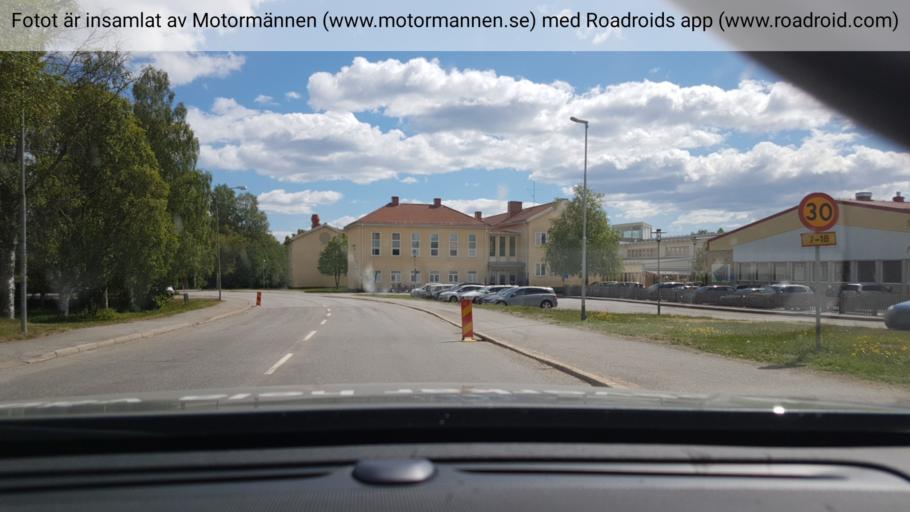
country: SE
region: Vaesterbotten
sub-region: Nordmalings Kommun
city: Nordmaling
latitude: 63.5691
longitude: 19.5043
